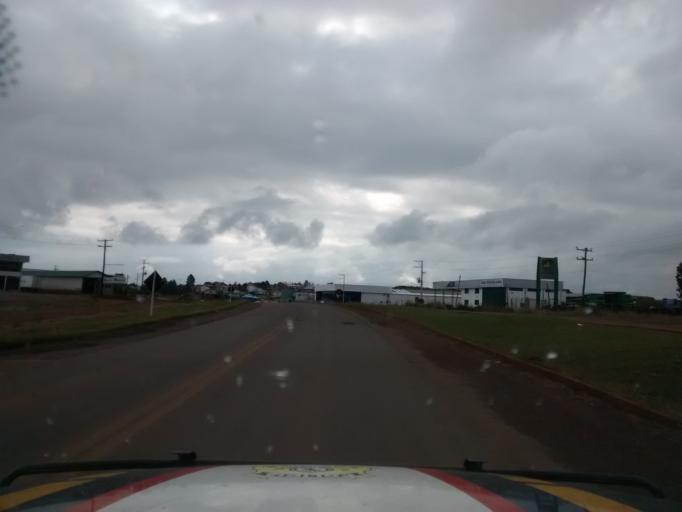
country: BR
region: Rio Grande do Sul
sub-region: Lagoa Vermelha
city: Lagoa Vermelha
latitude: -28.2110
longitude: -51.5111
